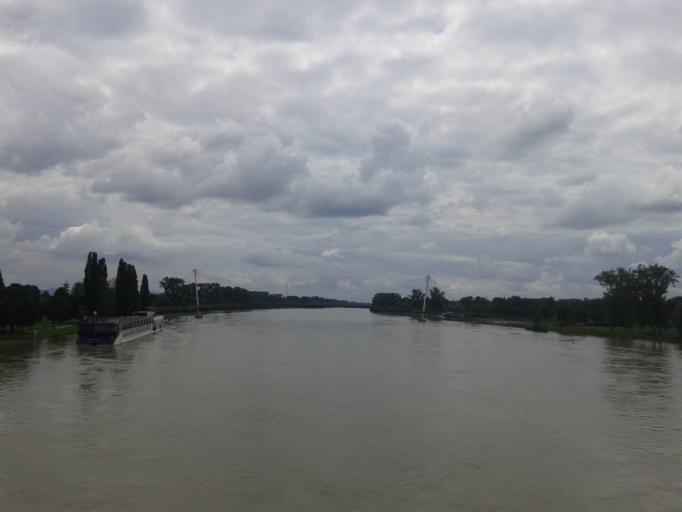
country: DE
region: Baden-Wuerttemberg
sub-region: Freiburg Region
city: Kehl
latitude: 48.5739
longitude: 7.8026
